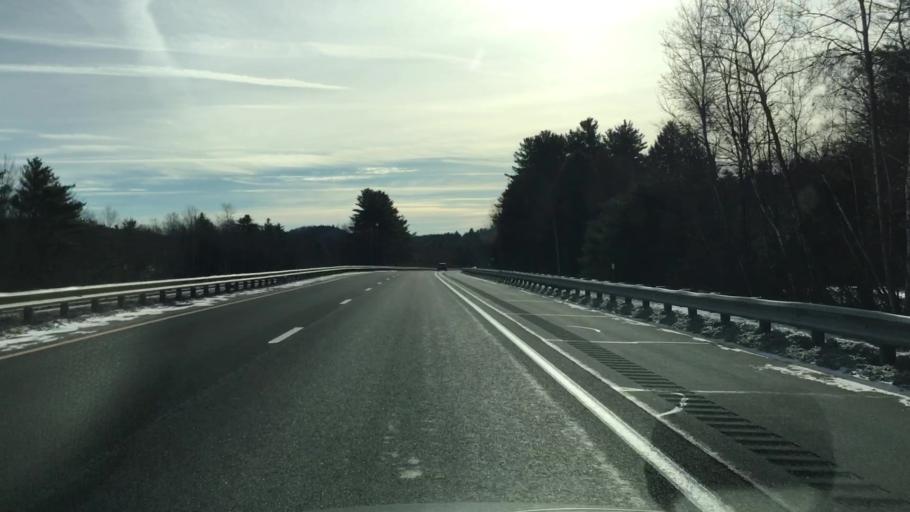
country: US
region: New Hampshire
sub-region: Sullivan County
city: Grantham
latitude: 43.5337
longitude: -72.1396
